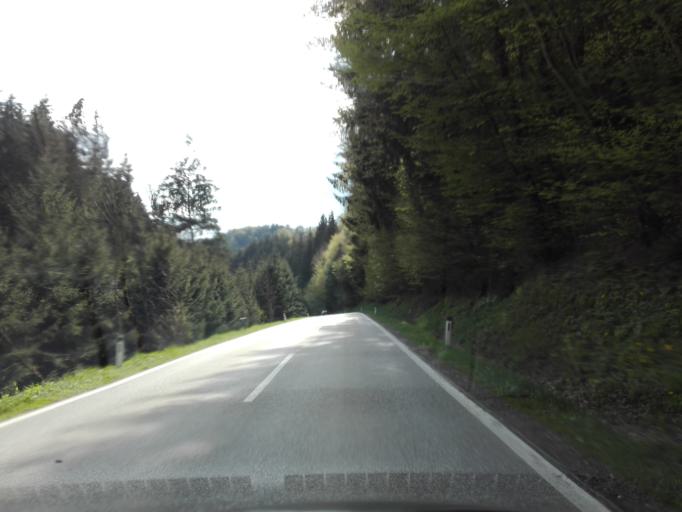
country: AT
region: Upper Austria
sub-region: Politischer Bezirk Urfahr-Umgebung
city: Feldkirchen an der Donau
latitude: 48.3822
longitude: 14.0668
